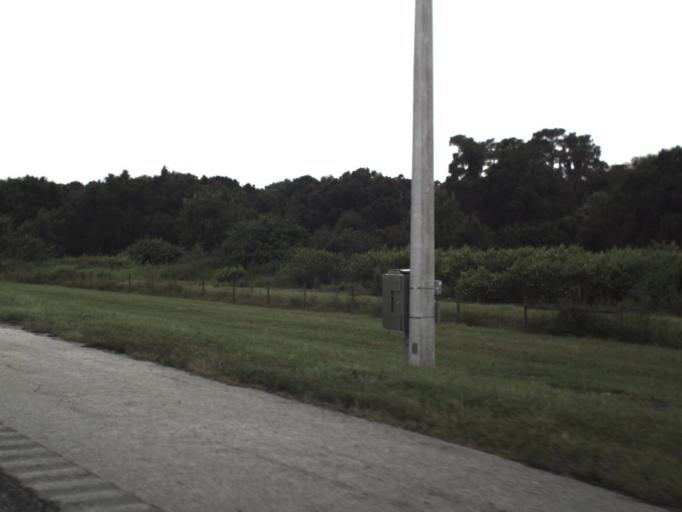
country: US
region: Florida
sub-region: Manatee County
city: Ellenton
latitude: 27.5602
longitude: -82.5132
